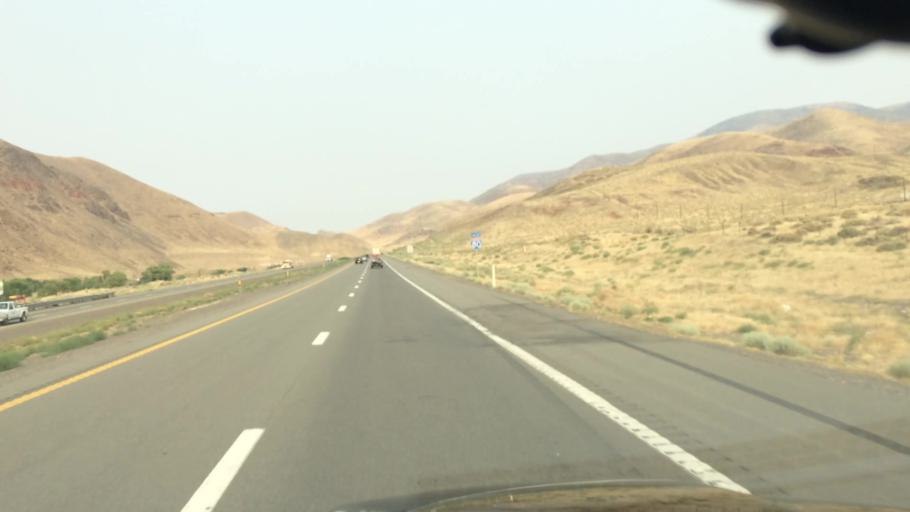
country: US
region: Nevada
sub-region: Lyon County
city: Fernley
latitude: 39.5894
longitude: -119.4338
